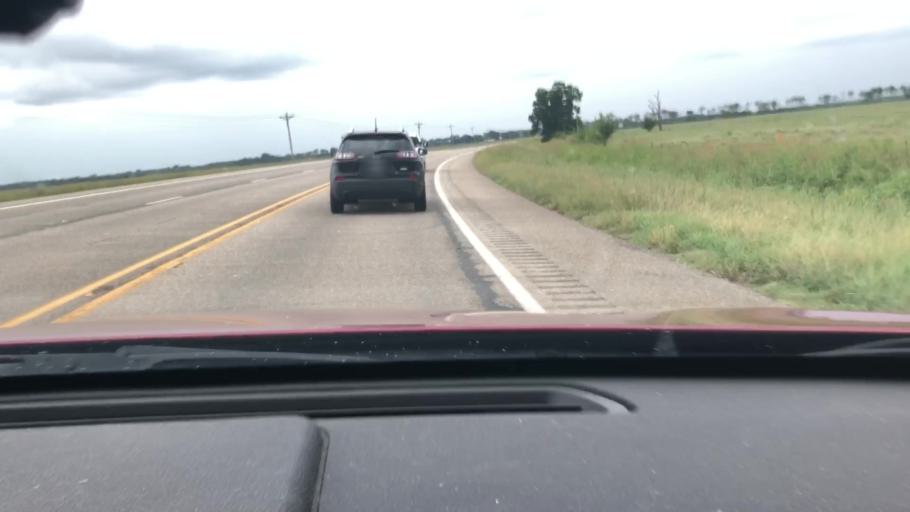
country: US
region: Arkansas
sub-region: Lafayette County
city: Lewisville
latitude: 33.3900
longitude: -93.7364
